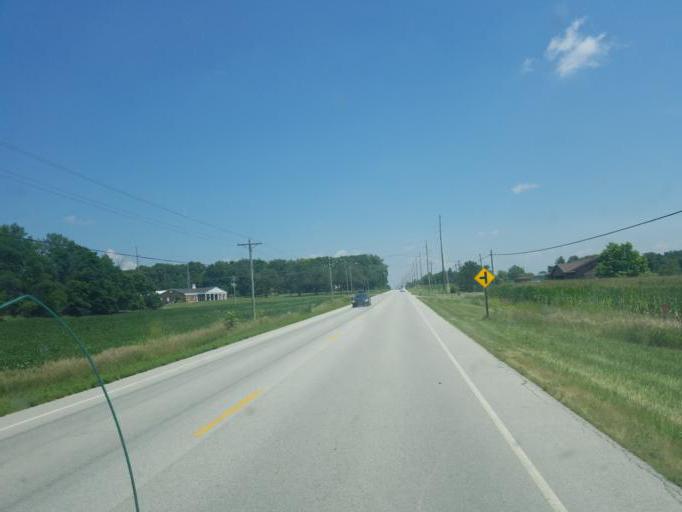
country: US
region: Ohio
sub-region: Auglaize County
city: Saint Marys
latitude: 40.5499
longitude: -84.3411
